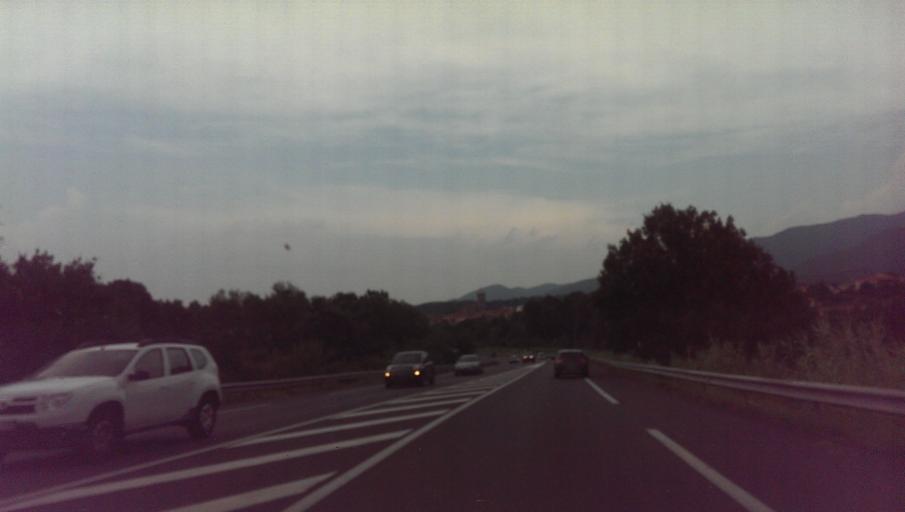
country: FR
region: Languedoc-Roussillon
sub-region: Departement des Pyrenees-Orientales
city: Vinca
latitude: 42.6469
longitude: 2.5192
